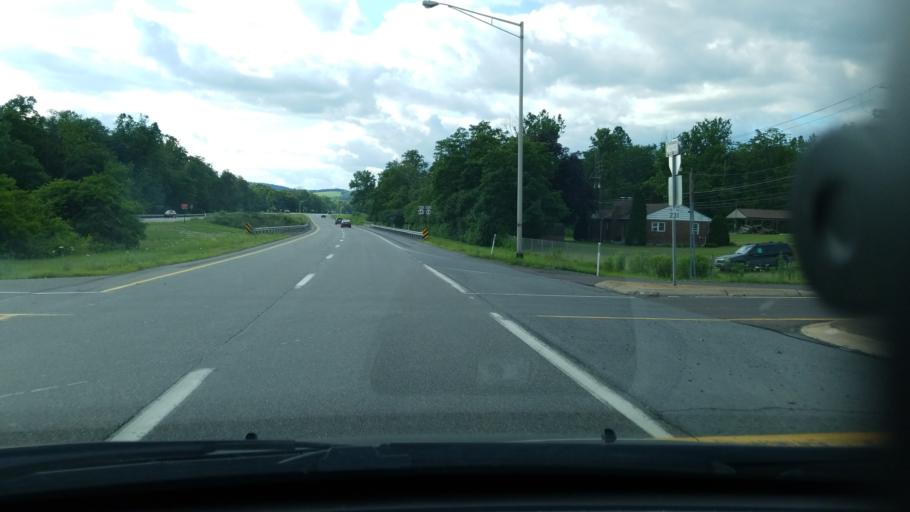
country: US
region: Pennsylvania
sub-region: Montour County
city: Danville
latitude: 40.9824
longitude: -76.6276
